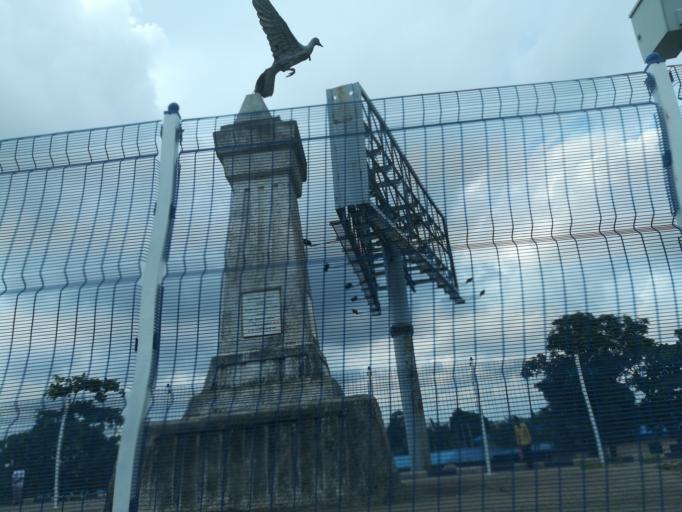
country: NG
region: Lagos
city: Ikeja
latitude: 6.5897
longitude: 3.3360
